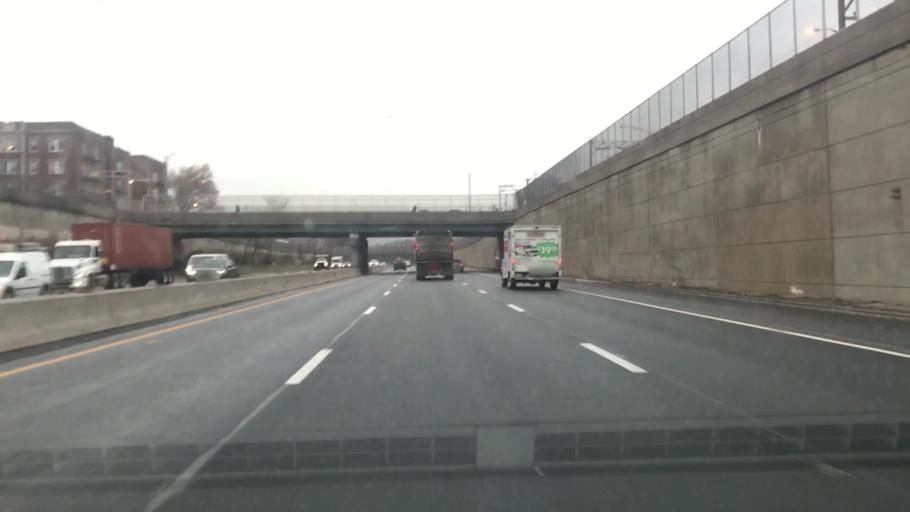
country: US
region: New Jersey
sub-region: Essex County
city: East Orange
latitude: 40.7628
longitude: -74.2150
